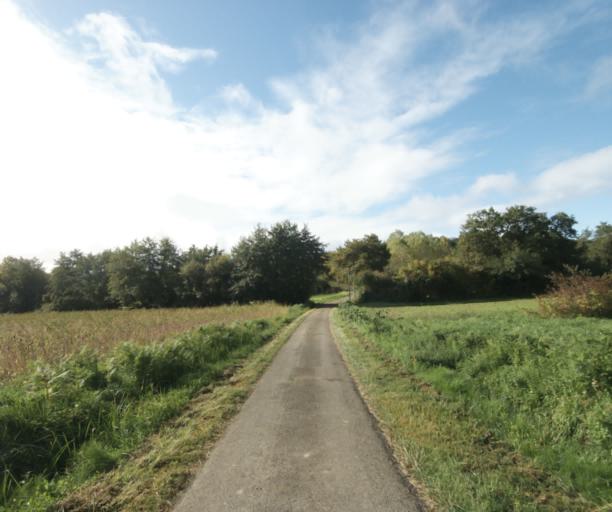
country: FR
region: Midi-Pyrenees
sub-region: Departement du Gers
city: Cazaubon
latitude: 43.8633
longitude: -0.0776
